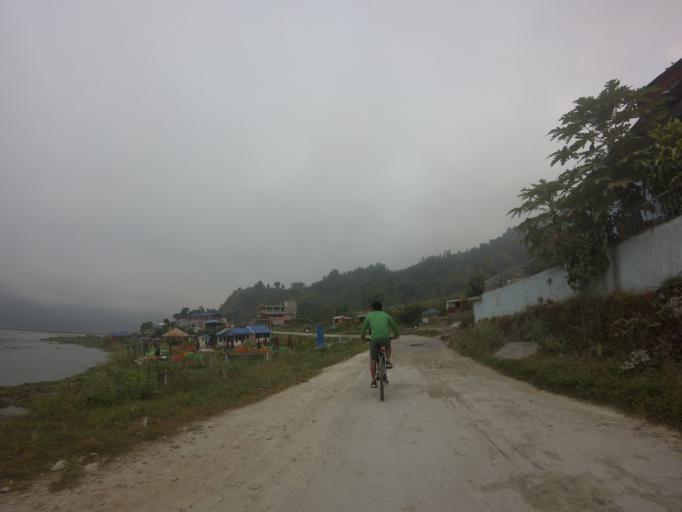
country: NP
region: Western Region
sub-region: Gandaki Zone
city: Pokhara
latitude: 28.2278
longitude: 83.9391
